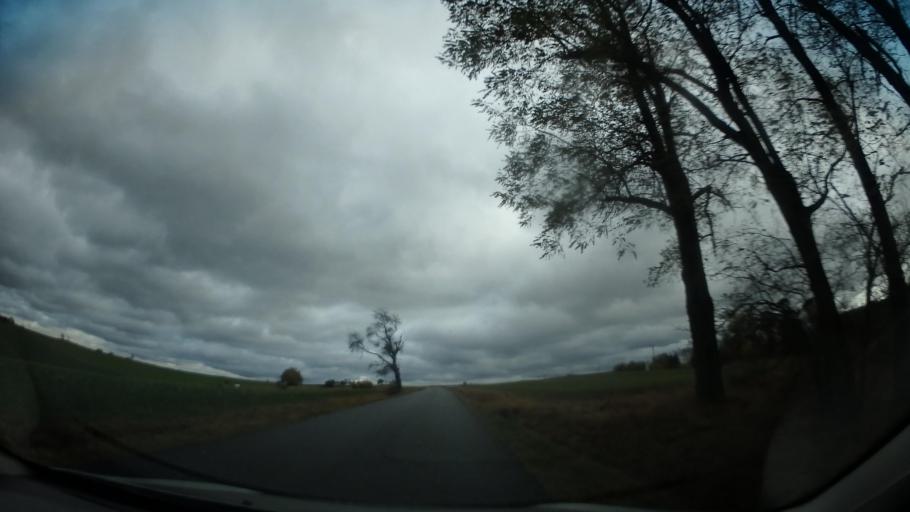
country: CZ
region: Vysocina
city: Namest' nad Oslavou
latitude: 49.2892
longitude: 16.1263
